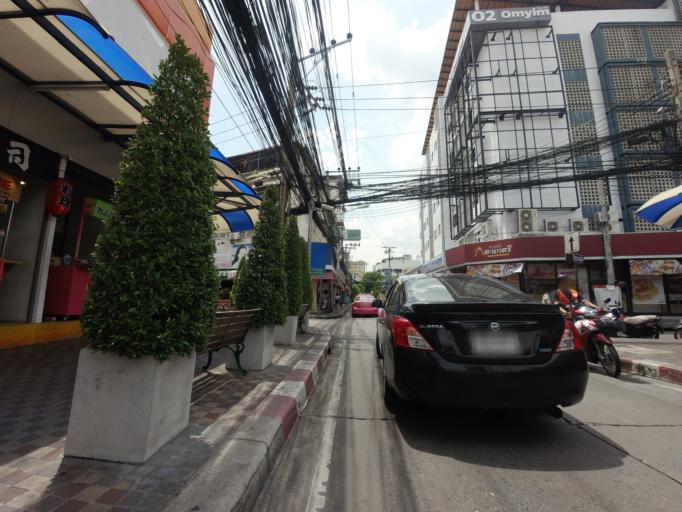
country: TH
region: Bangkok
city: Din Daeng
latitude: 13.7778
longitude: 100.5595
